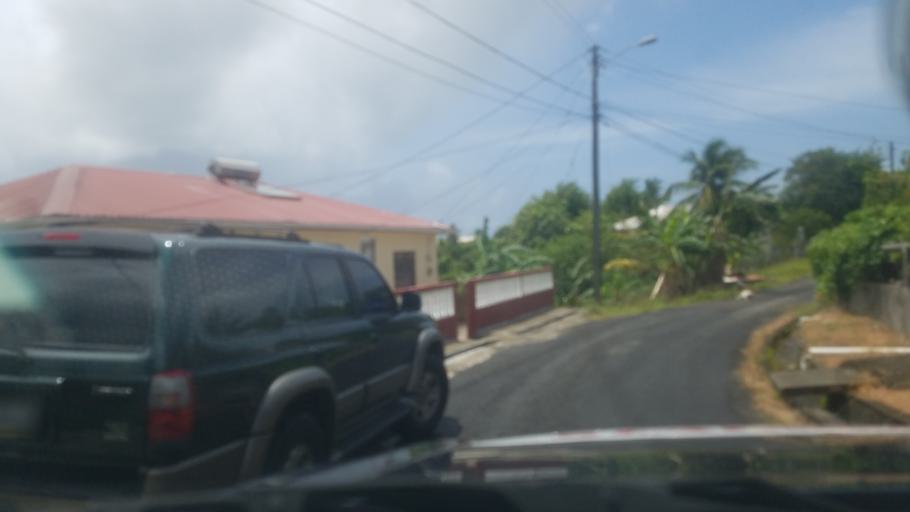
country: LC
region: Laborie Quarter
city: Laborie
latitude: 13.7526
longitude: -60.9671
